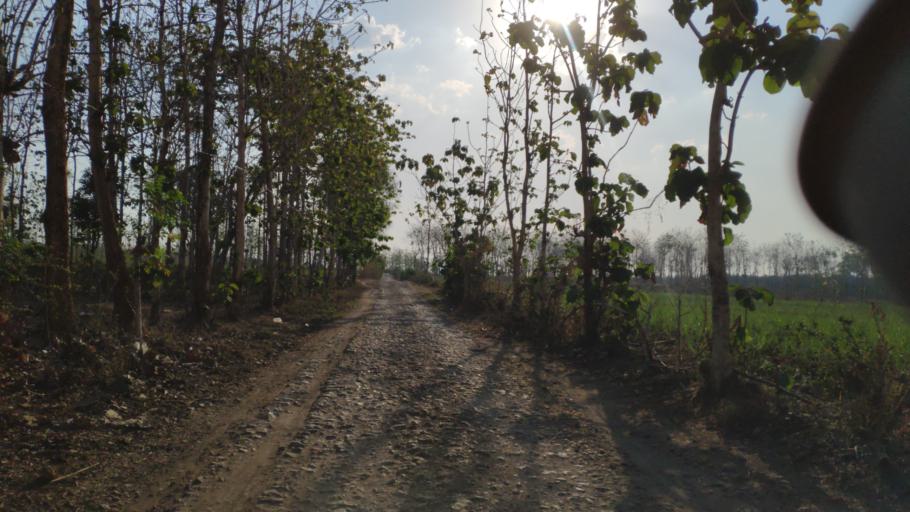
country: ID
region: Central Java
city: Pelem
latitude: -6.9951
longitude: 111.1924
